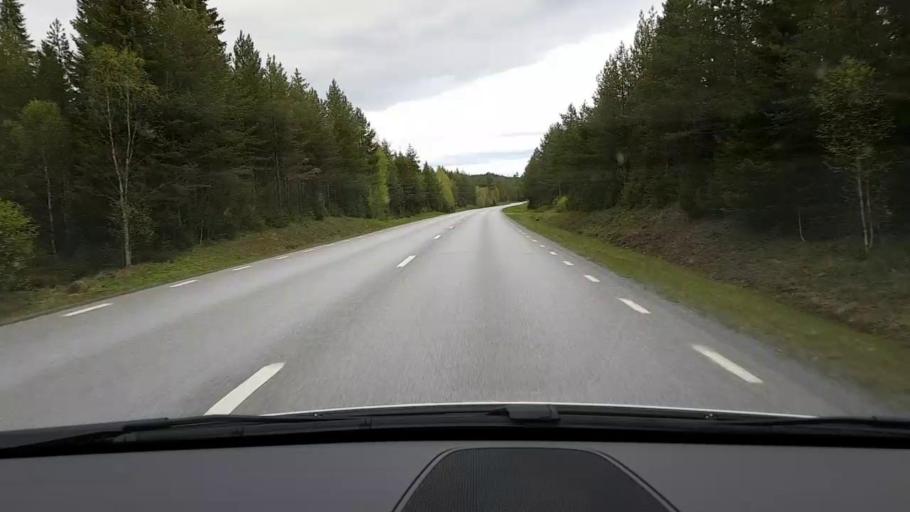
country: SE
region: Jaemtland
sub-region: Krokoms Kommun
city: Valla
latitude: 63.2880
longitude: 13.9280
